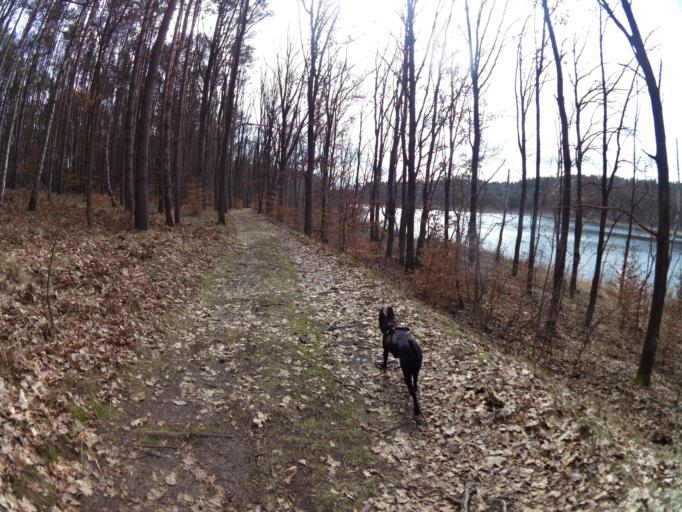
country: PL
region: West Pomeranian Voivodeship
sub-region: Powiat mysliborski
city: Mysliborz
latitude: 52.8483
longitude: 14.8368
